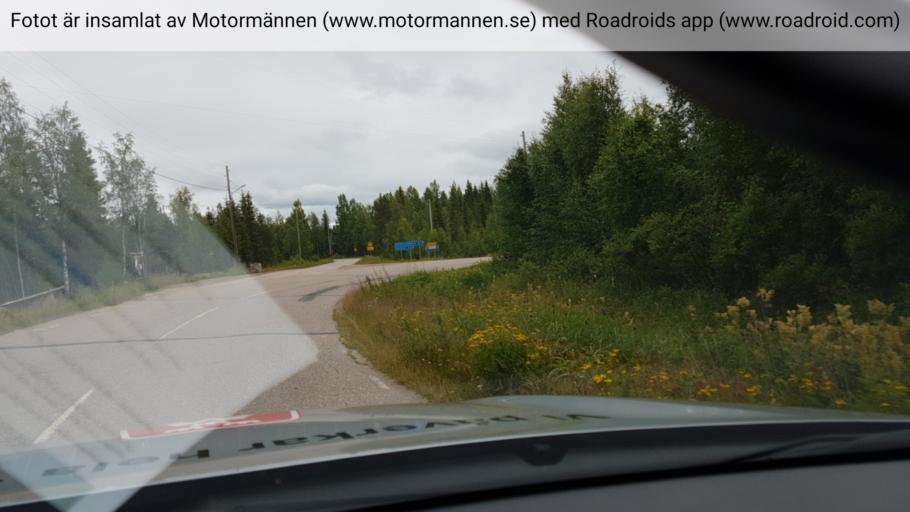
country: SE
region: Norrbotten
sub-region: Pajala Kommun
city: Pajala
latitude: 67.1765
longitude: 22.6443
